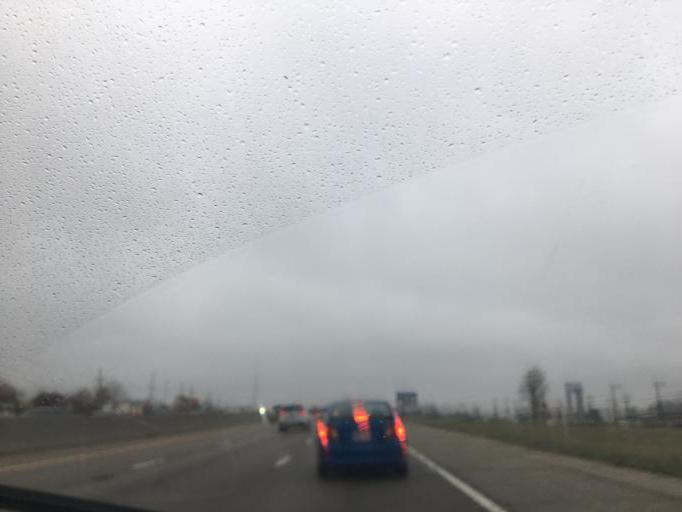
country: US
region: Kansas
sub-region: Johnson County
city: Olathe
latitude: 38.8943
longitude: -94.7881
